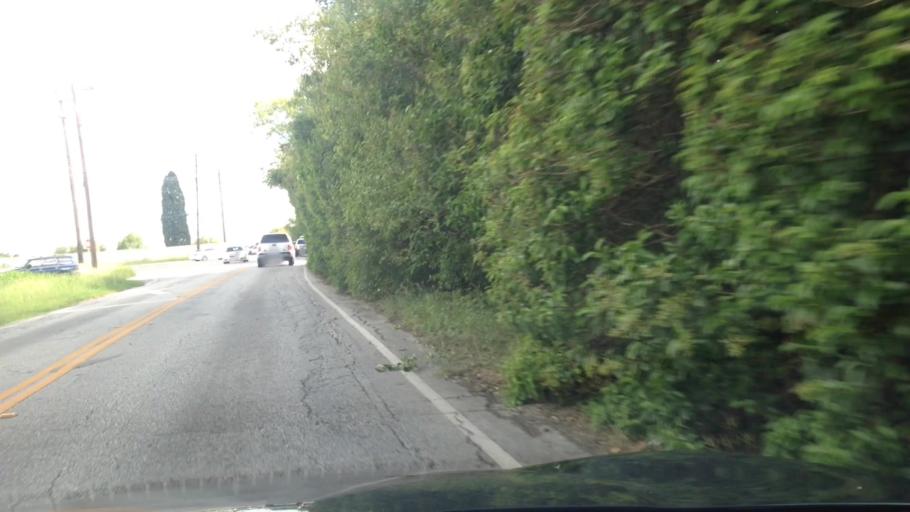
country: US
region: Texas
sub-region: Bexar County
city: Live Oak
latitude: 29.5791
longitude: -98.4021
